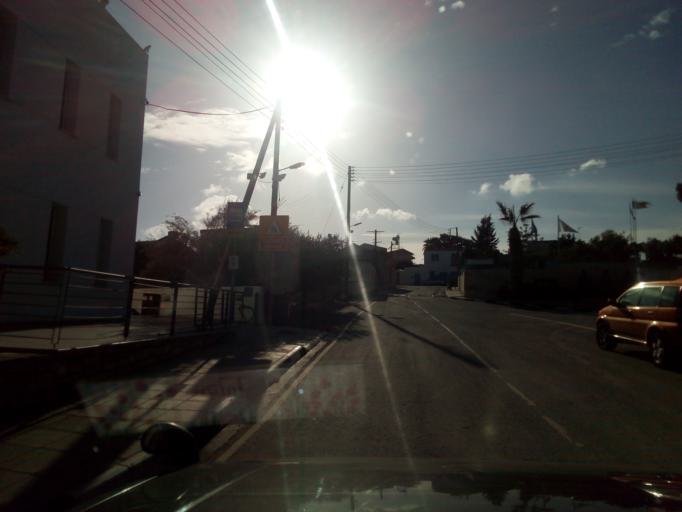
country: CY
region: Larnaka
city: Kofinou
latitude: 34.8072
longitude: 33.4345
